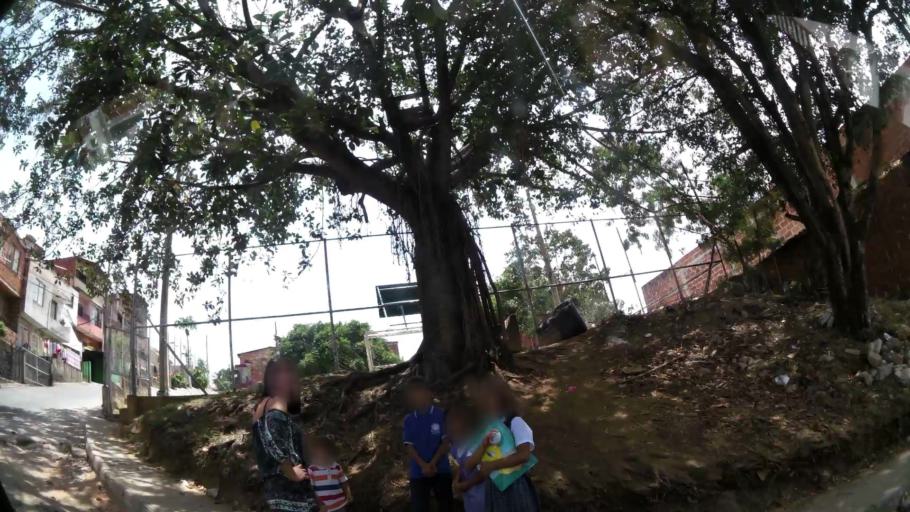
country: CO
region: Antioquia
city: Bello
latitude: 6.3498
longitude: -75.5617
